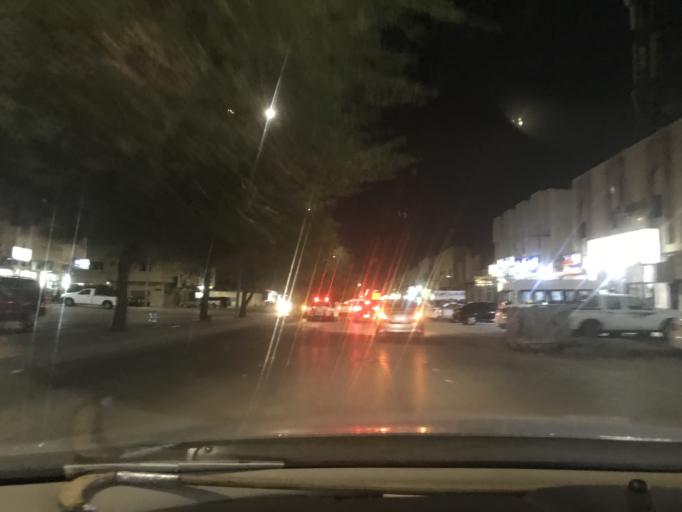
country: SA
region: Ar Riyad
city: Riyadh
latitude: 24.7377
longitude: 46.7756
